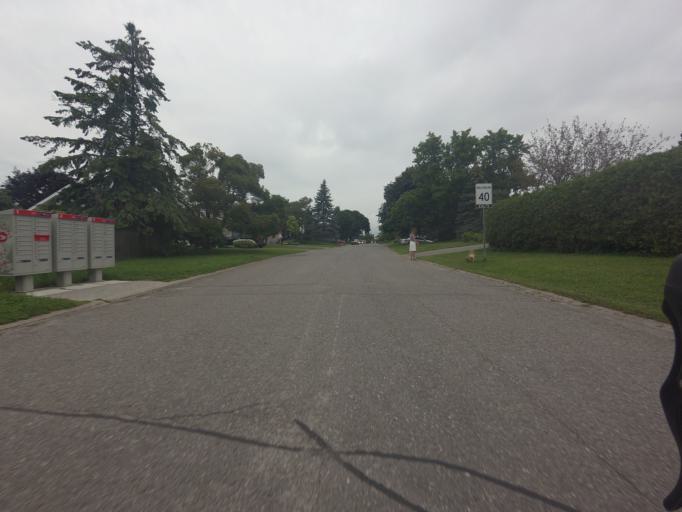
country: CA
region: Ontario
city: Ottawa
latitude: 45.3483
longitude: -75.7474
